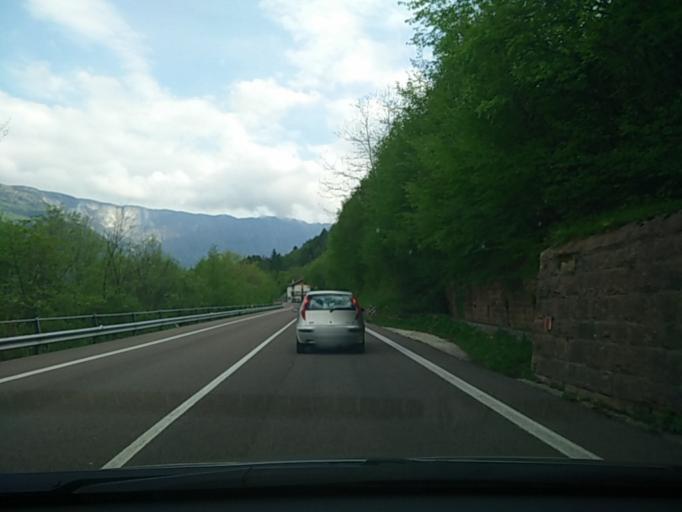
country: IT
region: Veneto
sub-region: Provincia di Belluno
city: Farra d'Alpago
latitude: 46.1177
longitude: 12.3237
